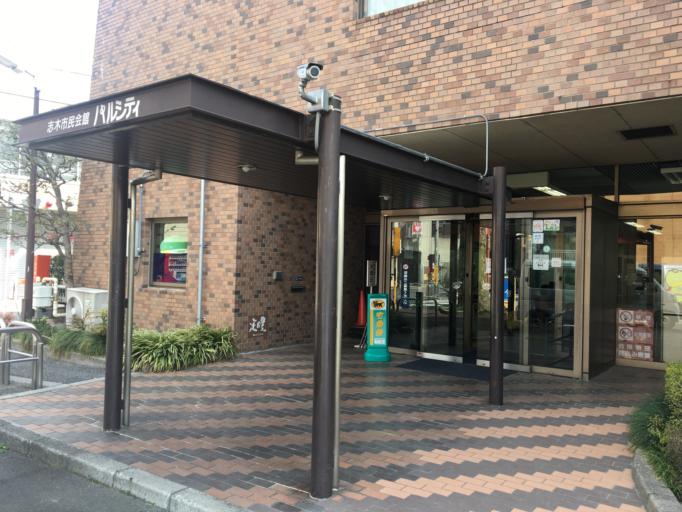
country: JP
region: Saitama
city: Shiki
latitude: 35.8312
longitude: 139.5772
